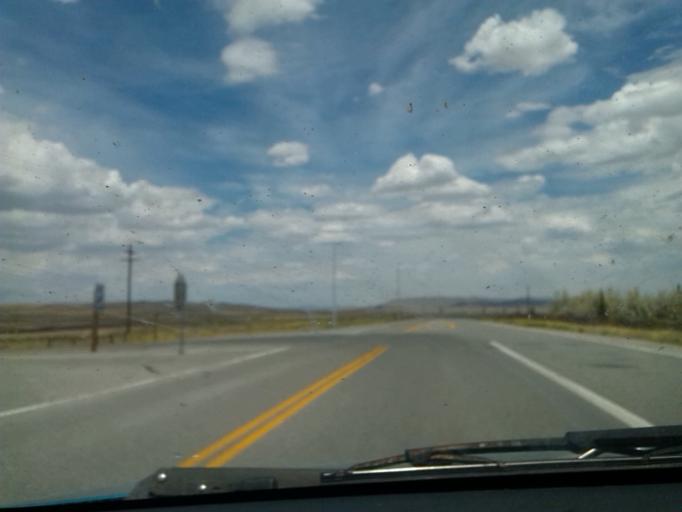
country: US
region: Wyoming
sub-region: Carbon County
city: Rawlins
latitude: 41.7812
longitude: -107.1232
